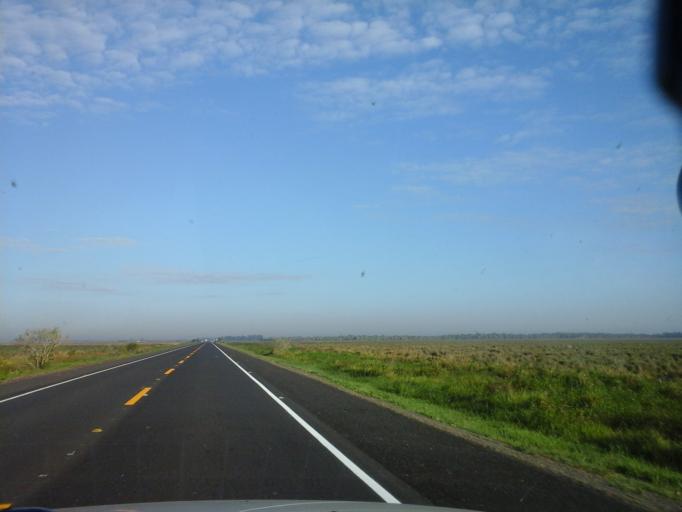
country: PY
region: Neembucu
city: Cerrito
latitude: -26.8681
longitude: -57.7792
